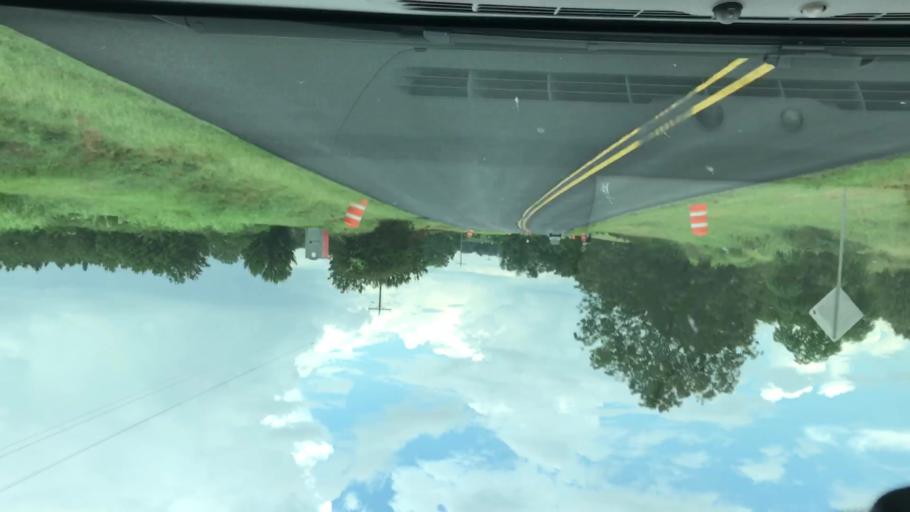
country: US
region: Georgia
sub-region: Early County
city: Blakely
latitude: 31.4218
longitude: -84.9641
